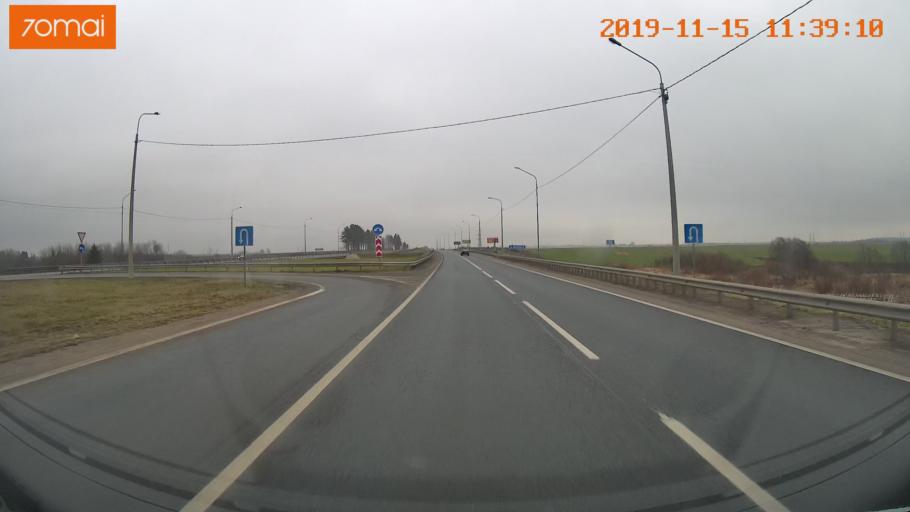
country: RU
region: Vologda
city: Molochnoye
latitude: 59.2110
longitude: 39.7168
